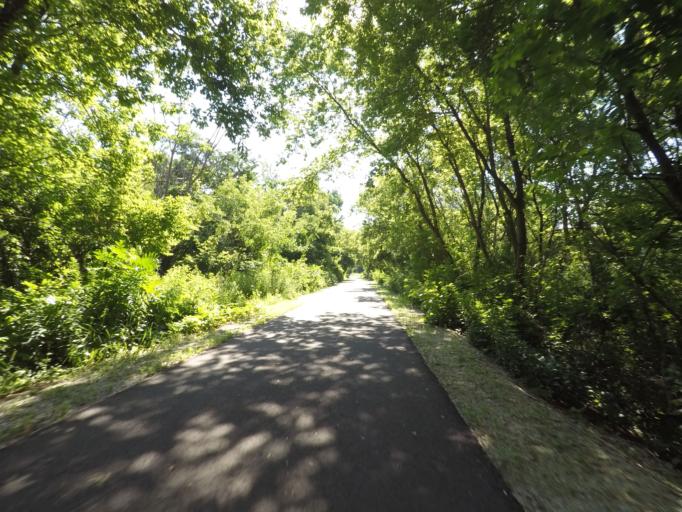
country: US
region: Wisconsin
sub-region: Milwaukee County
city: West Allis
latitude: 43.0257
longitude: -88.0411
